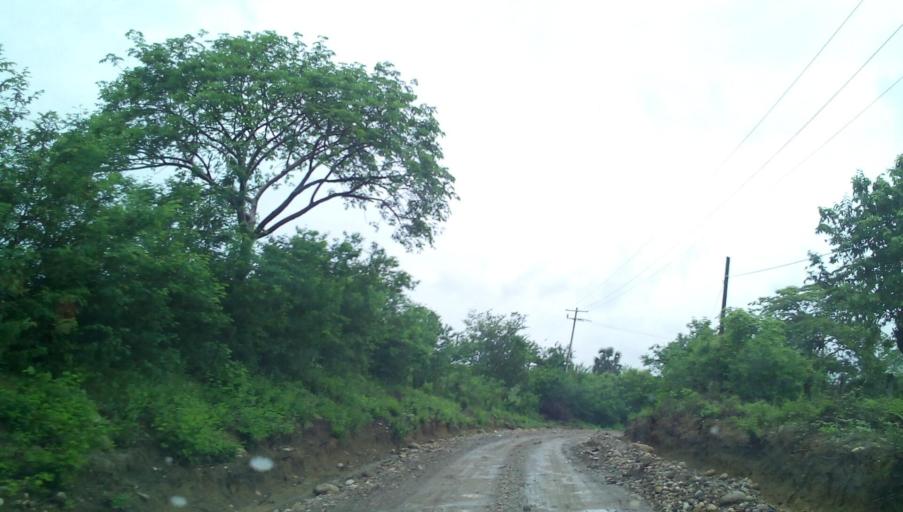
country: MX
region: Veracruz
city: Tempoal de Sanchez
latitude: 21.4451
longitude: -98.4232
